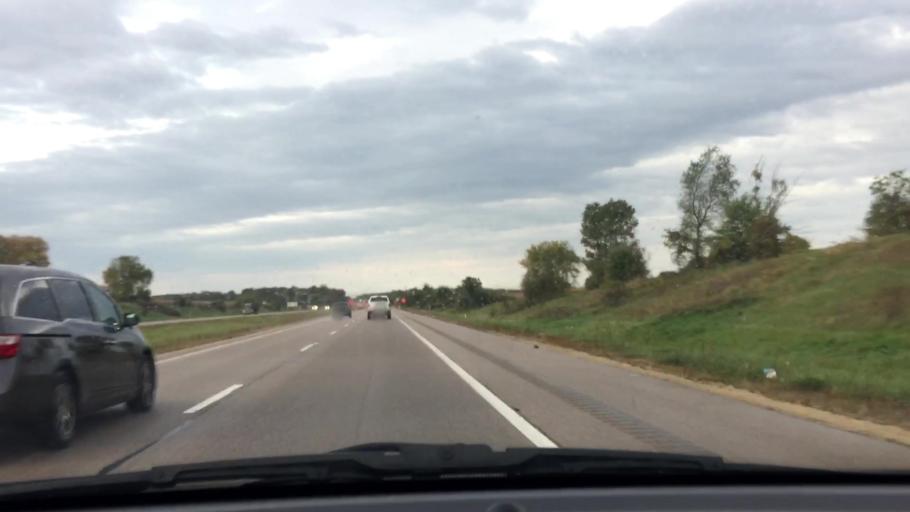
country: US
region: Wisconsin
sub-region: Rock County
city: Clinton
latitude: 42.5521
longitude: -88.9284
